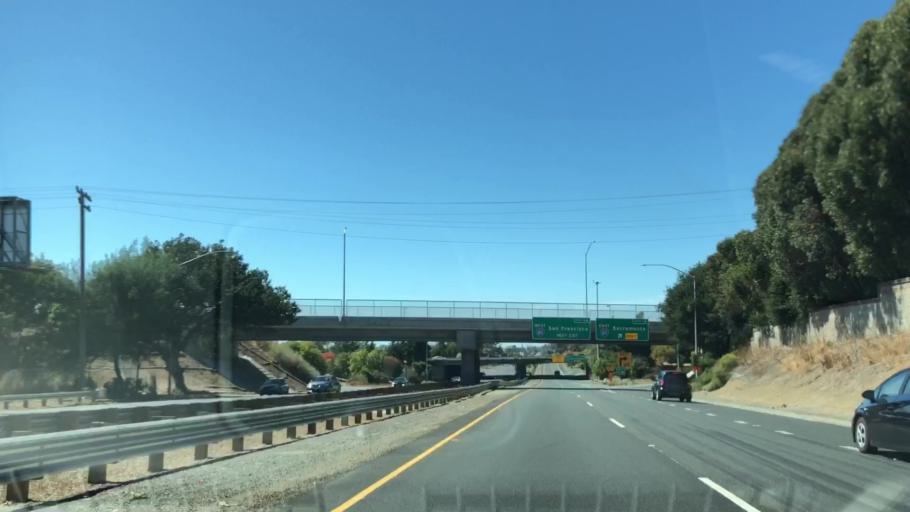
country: US
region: California
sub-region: Solano County
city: Vallejo
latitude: 38.0908
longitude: -122.2274
